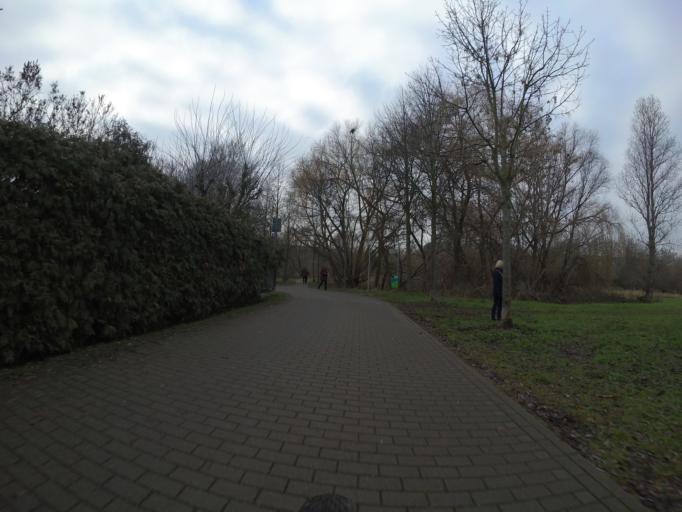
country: DE
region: Brandenburg
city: Ahrensfelde
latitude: 52.5681
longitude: 13.5842
